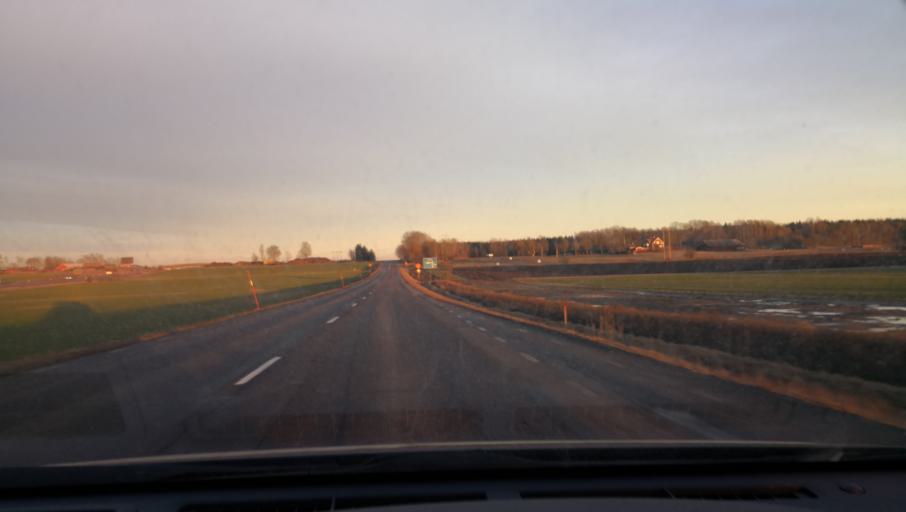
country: SE
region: OErebro
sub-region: Orebro Kommun
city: Vintrosa
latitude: 59.2444
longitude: 14.9624
